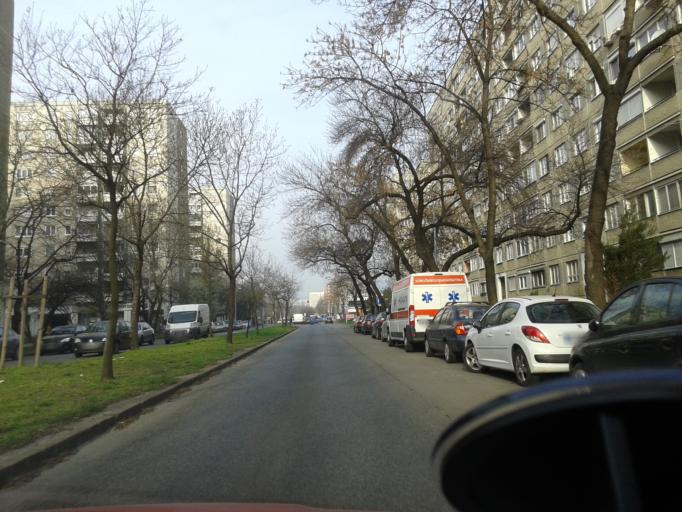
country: HU
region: Budapest
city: Budapest XI. keruelet
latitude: 47.4634
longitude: 19.0364
